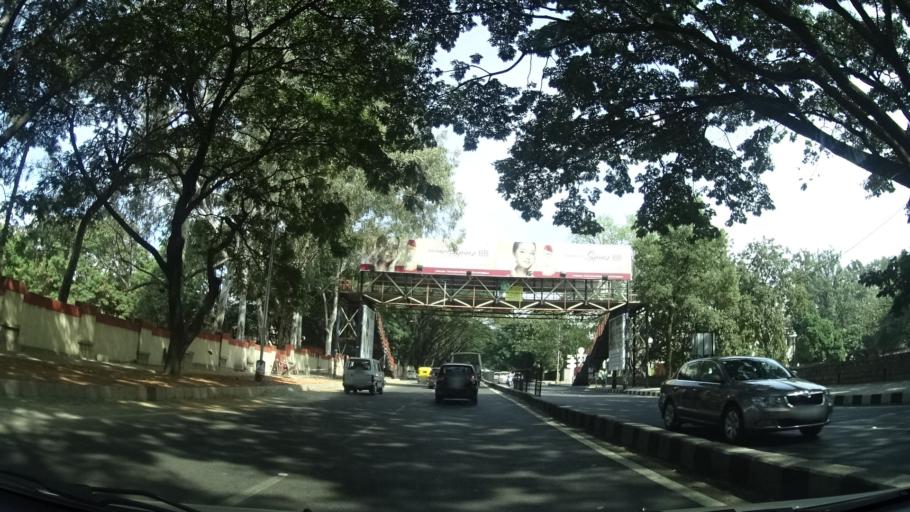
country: IN
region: Karnataka
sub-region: Bangalore Urban
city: Bangalore
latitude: 13.0150
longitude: 77.5750
